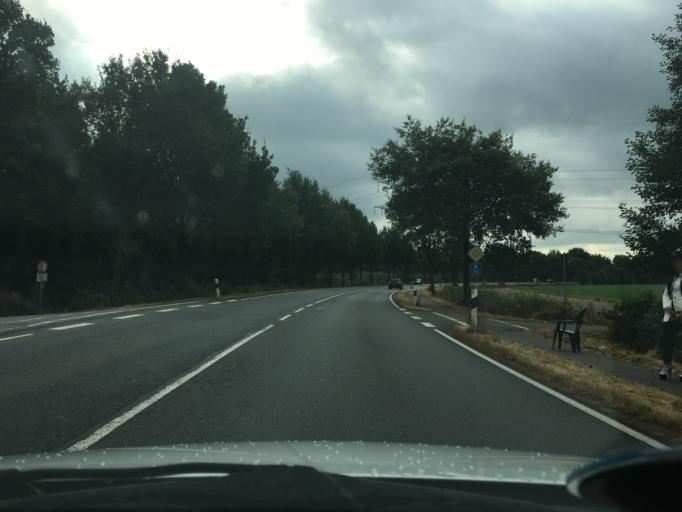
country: DE
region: Lower Saxony
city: Alfhausen
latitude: 52.4616
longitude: 7.9629
